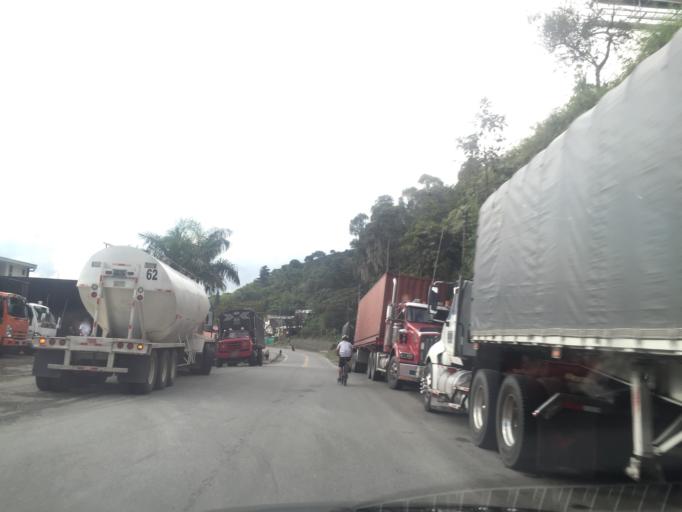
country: CO
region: Quindio
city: Calarca
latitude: 4.5312
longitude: -75.6341
